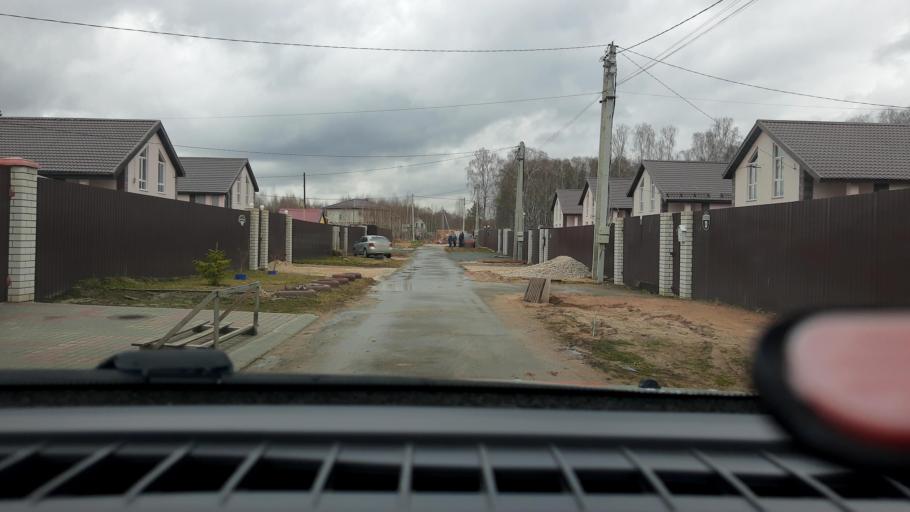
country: RU
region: Nizjnij Novgorod
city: Neklyudovo
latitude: 56.4114
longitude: 44.0211
